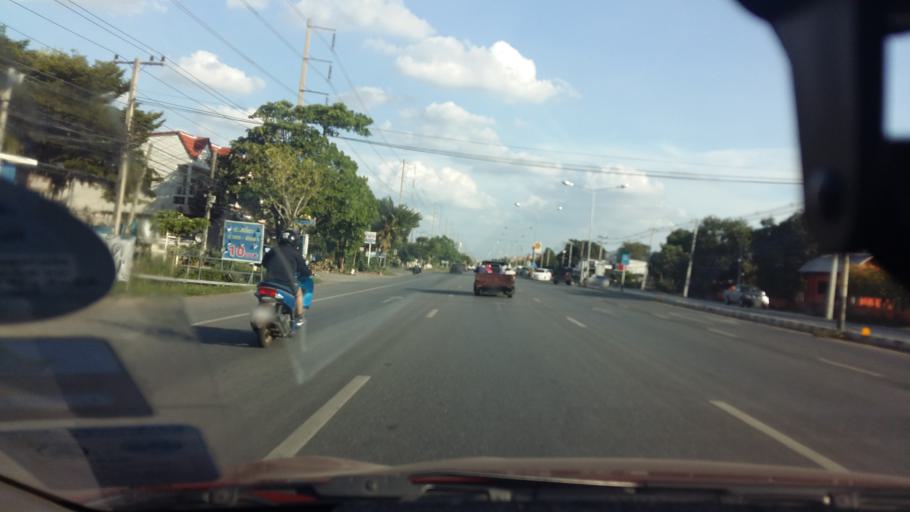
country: TH
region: Lop Buri
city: Lop Buri
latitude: 14.8351
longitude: 100.6453
